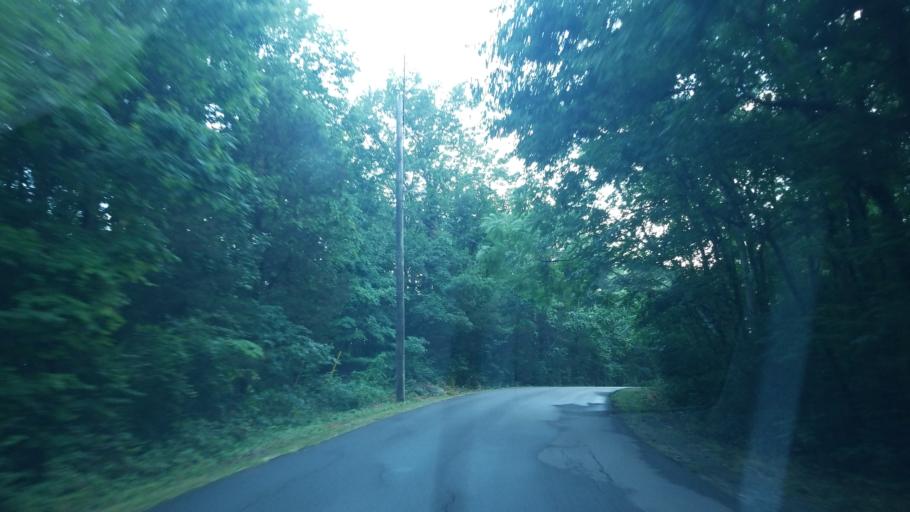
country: US
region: Tennessee
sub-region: Rutherford County
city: La Vergne
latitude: 36.1081
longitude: -86.6243
